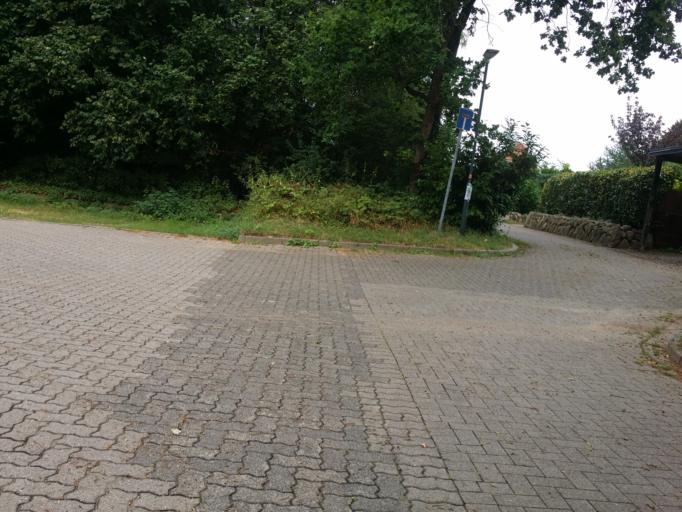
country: DE
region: Schleswig-Holstein
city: Oldendorf
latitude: 53.9482
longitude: 9.4593
